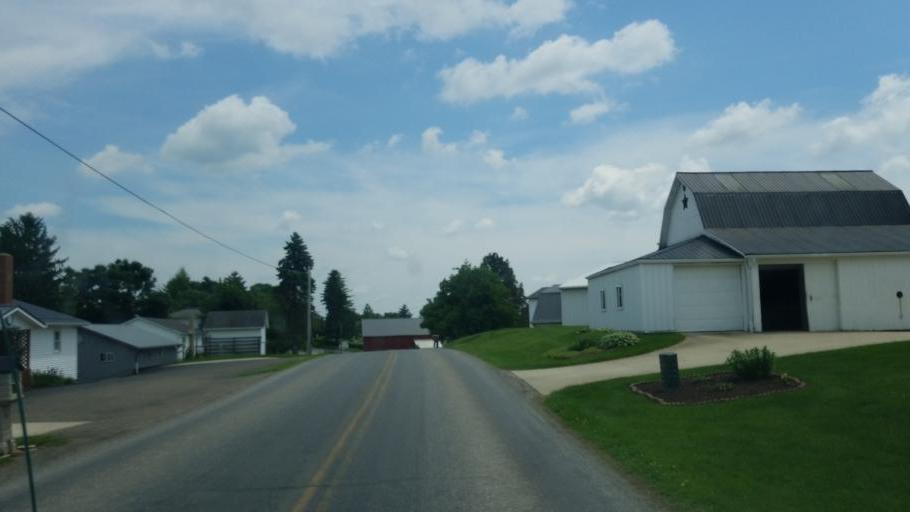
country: US
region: Ohio
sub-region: Tuscarawas County
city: Sugarcreek
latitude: 40.4474
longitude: -81.7681
